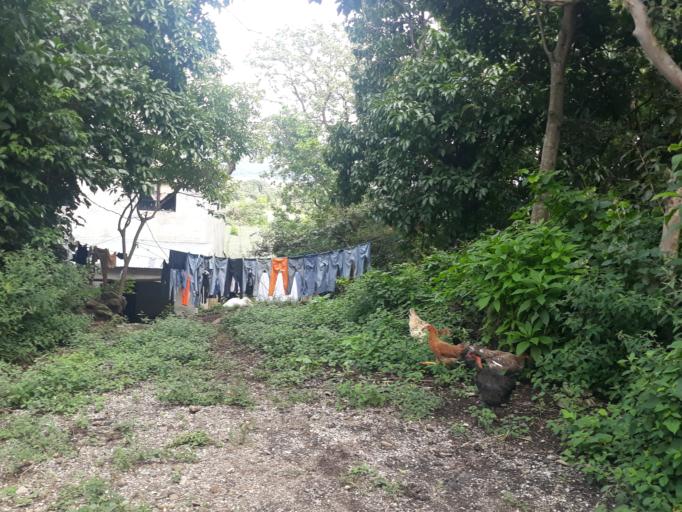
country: GT
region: Escuintla
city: San Vicente Pacaya
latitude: 14.3709
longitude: -90.5554
